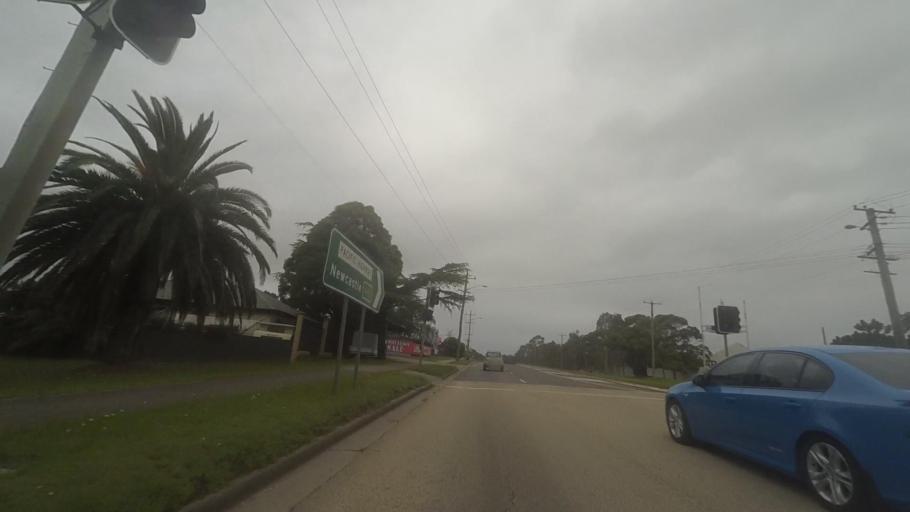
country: AU
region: New South Wales
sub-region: Newcastle
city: Mayfield West
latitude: -32.8708
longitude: 151.7102
